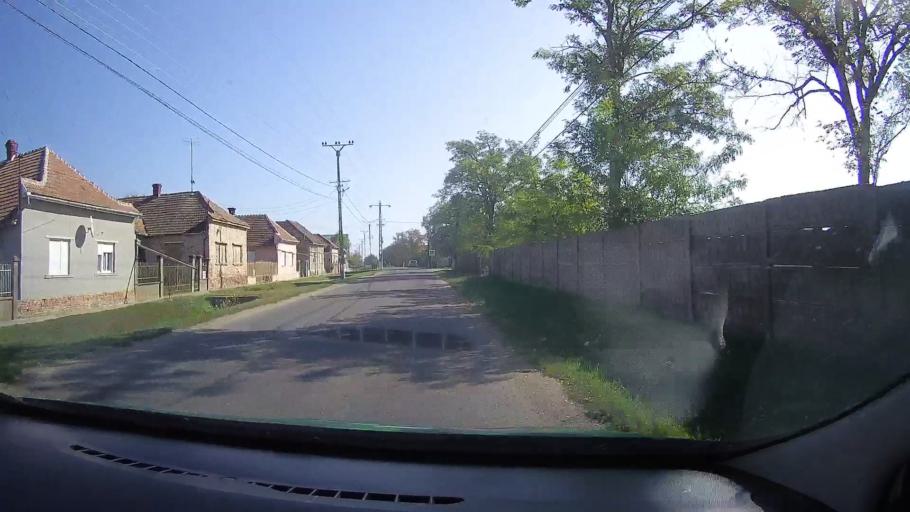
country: RO
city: Foieni
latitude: 47.6955
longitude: 22.3961
